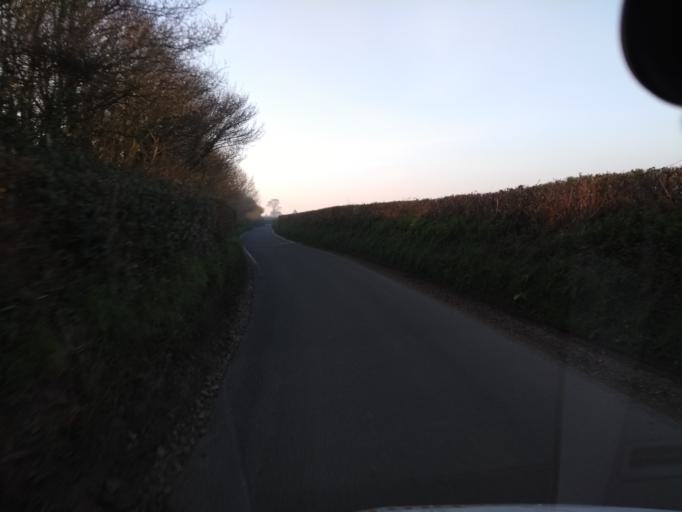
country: GB
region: England
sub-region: Somerset
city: Ilminster
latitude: 50.8470
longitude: -2.8829
